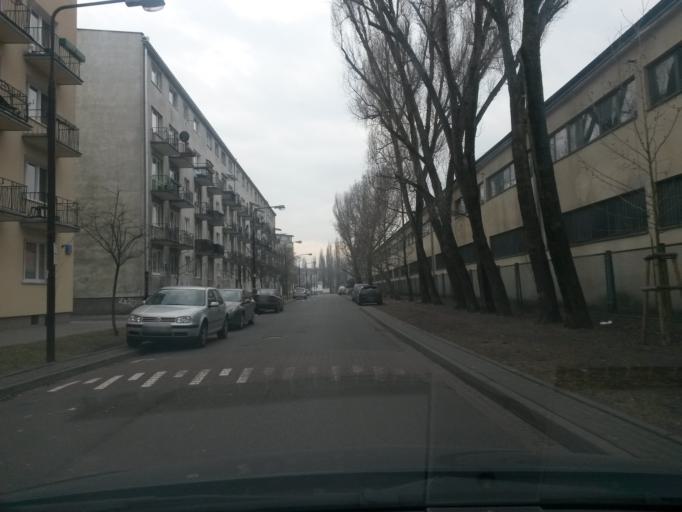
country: PL
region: Masovian Voivodeship
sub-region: Warszawa
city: Mokotow
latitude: 52.2119
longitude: 21.0455
